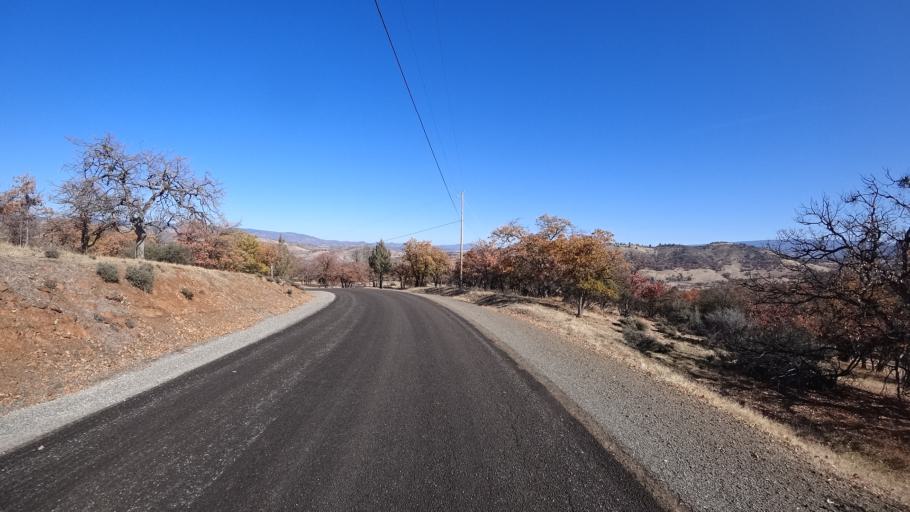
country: US
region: California
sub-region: Siskiyou County
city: Montague
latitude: 41.8796
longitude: -122.4890
